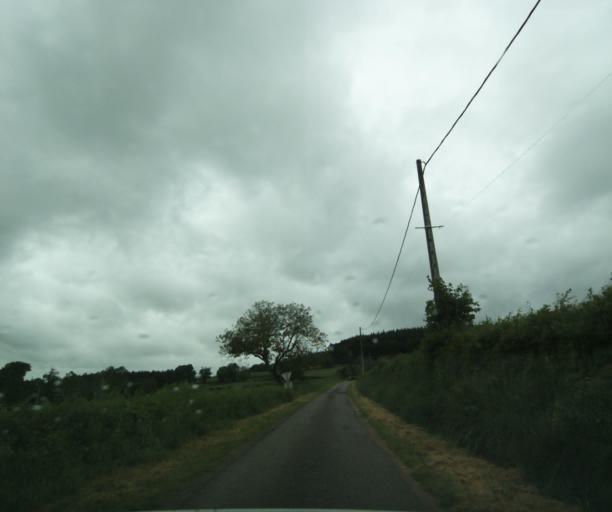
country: FR
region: Bourgogne
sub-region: Departement de Saone-et-Loire
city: Charolles
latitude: 46.4592
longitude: 4.4209
